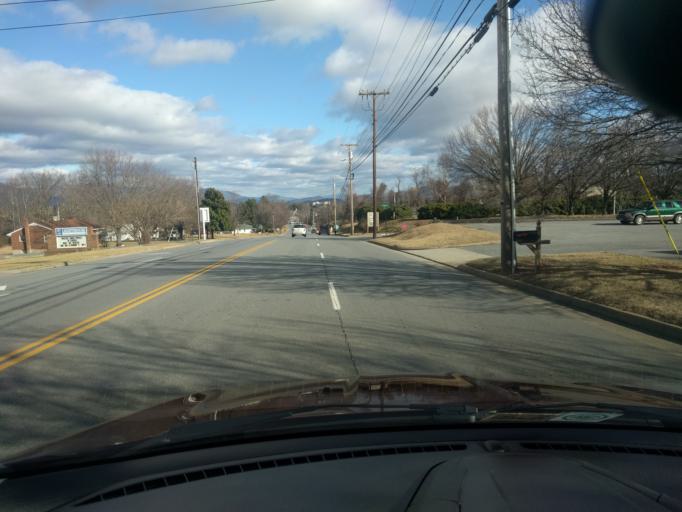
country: US
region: Virginia
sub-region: City of Bedford
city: Bedford
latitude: 37.3168
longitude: -79.5368
